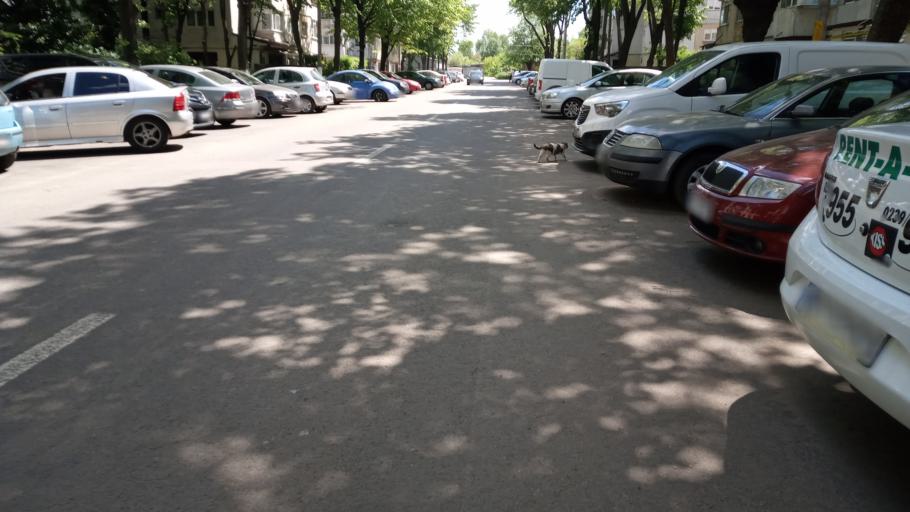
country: RO
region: Braila
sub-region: Municipiul Braila
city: Braila
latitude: 45.2919
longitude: 27.9671
